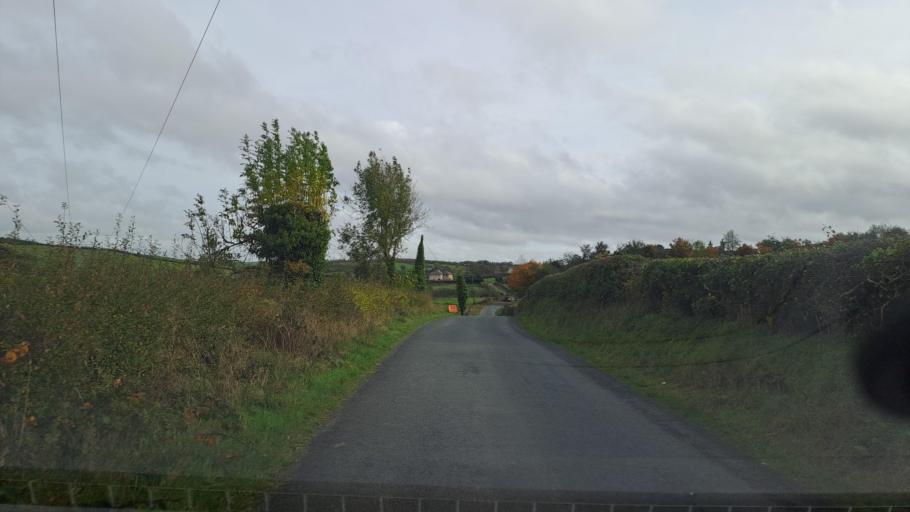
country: IE
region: Ulster
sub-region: An Cabhan
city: Bailieborough
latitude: 54.0213
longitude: -6.9153
